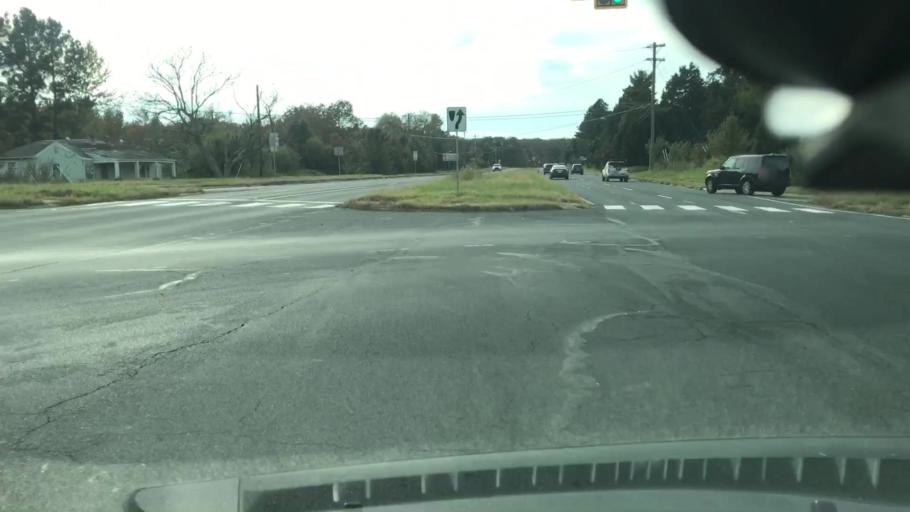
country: US
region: Virginia
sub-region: Fairfax County
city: Fairfax Station
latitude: 38.8282
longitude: -77.3682
